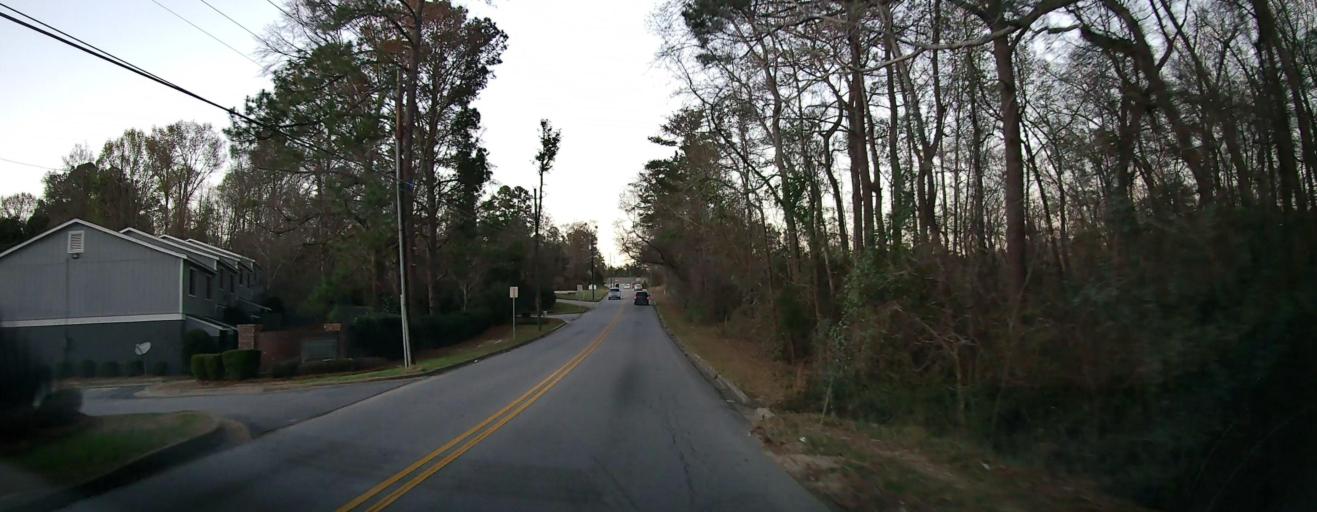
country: US
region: Alabama
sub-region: Russell County
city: Phenix City
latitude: 32.4897
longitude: -85.0195
